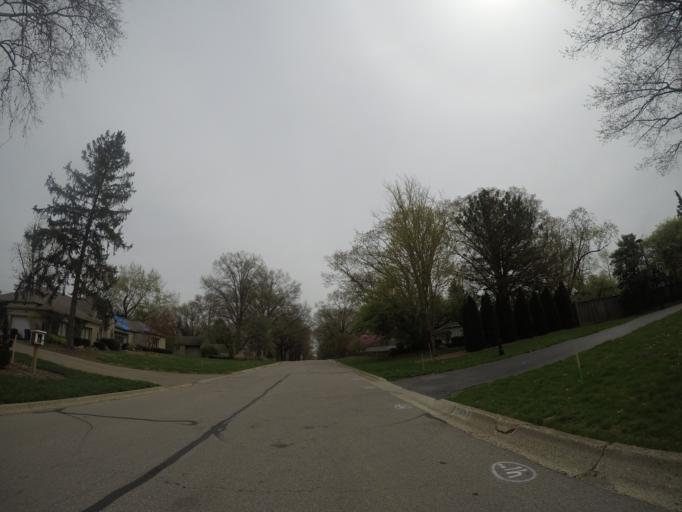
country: US
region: Ohio
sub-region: Franklin County
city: Upper Arlington
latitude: 40.0147
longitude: -83.0783
